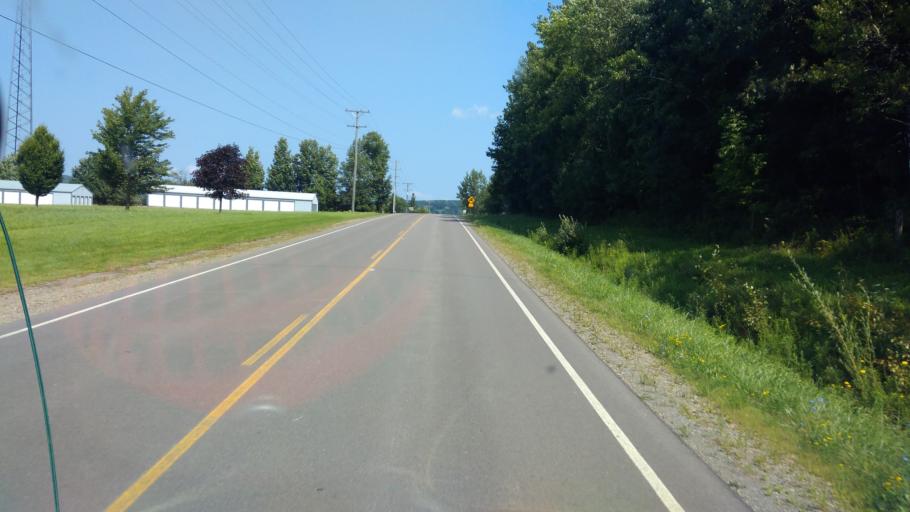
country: US
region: New York
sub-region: Allegany County
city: Belmont
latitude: 42.2944
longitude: -78.0263
